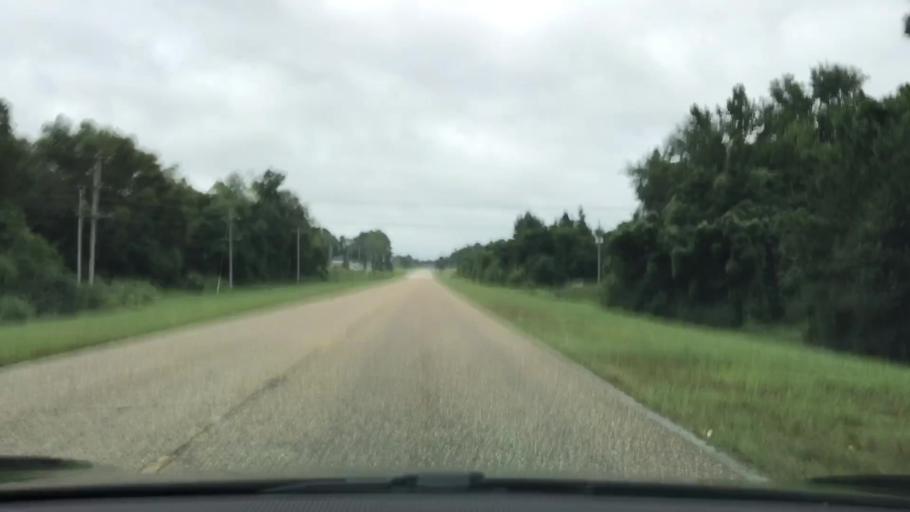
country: US
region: Alabama
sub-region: Coffee County
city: Elba
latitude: 31.4082
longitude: -86.0828
